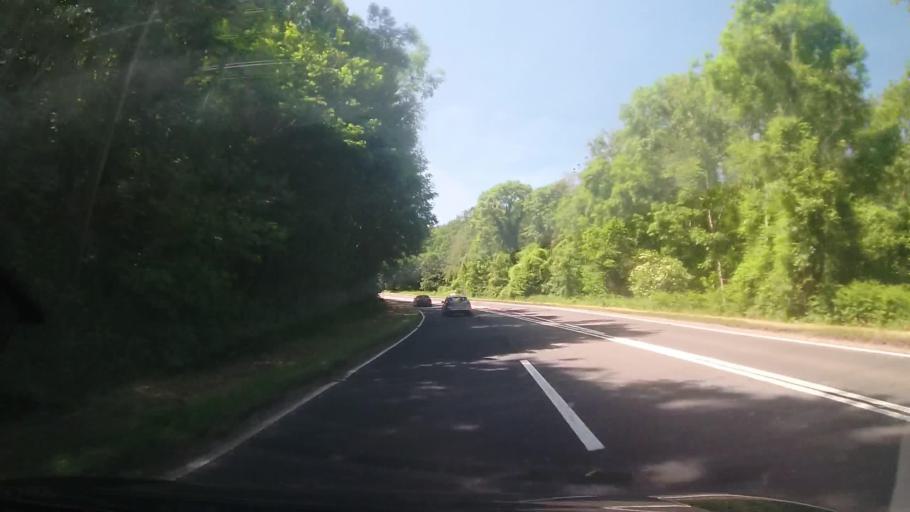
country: GB
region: England
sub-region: Herefordshire
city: Hope under Dinmore
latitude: 52.1624
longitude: -2.7198
